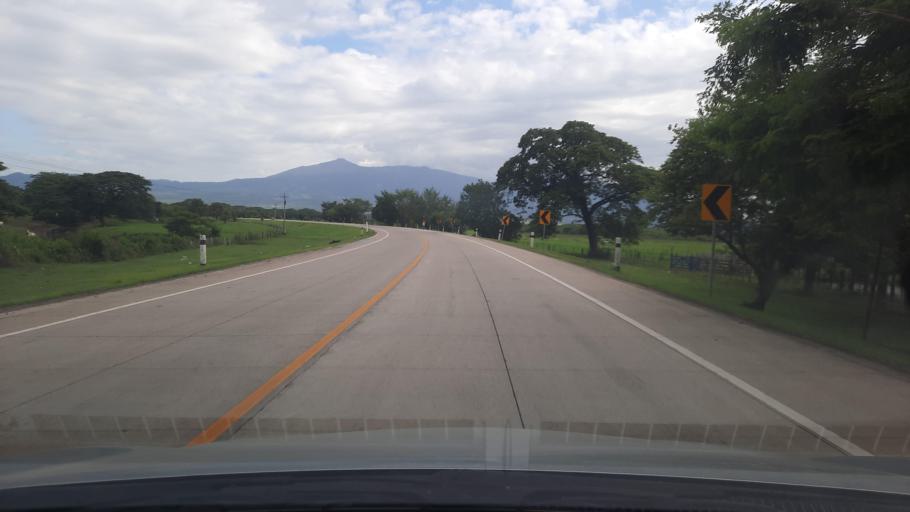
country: NI
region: Chinandega
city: Somotillo
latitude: 12.8152
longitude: -86.9014
